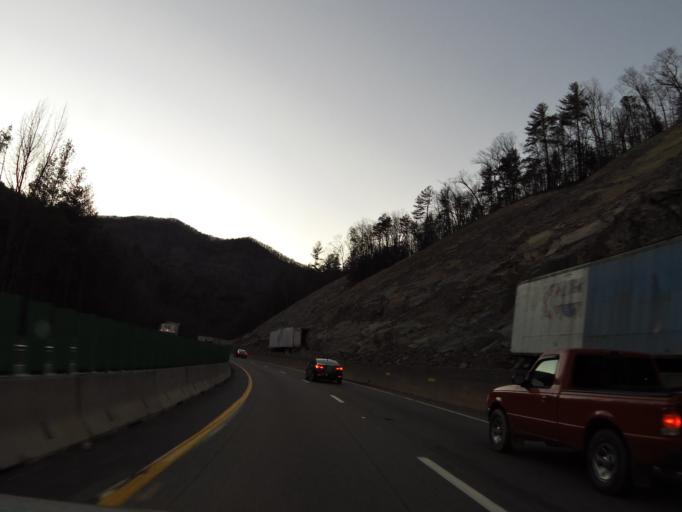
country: US
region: North Carolina
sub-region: Haywood County
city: Cove Creek
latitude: 35.7393
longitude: -83.0266
